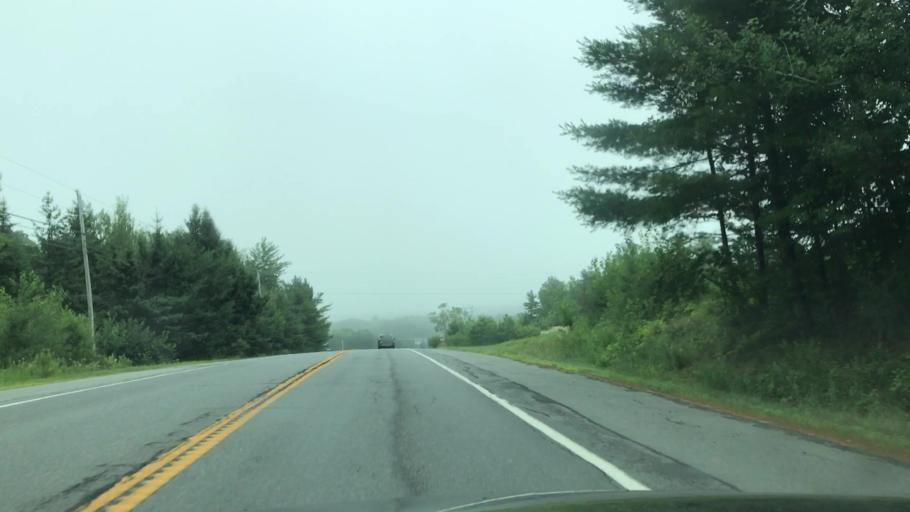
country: US
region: Maine
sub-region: Lincoln County
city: Nobleboro
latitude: 44.1039
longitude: -69.4351
